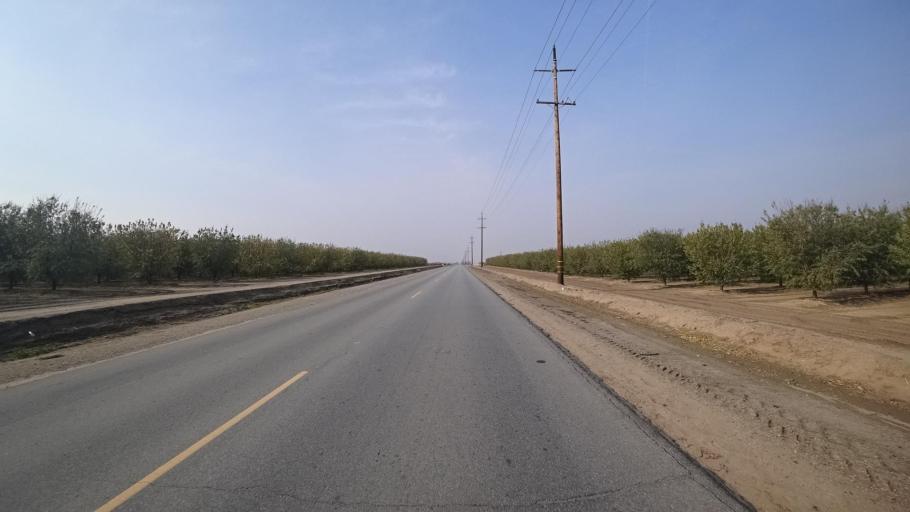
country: US
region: California
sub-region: Kern County
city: Weedpatch
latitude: 35.0956
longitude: -119.0003
